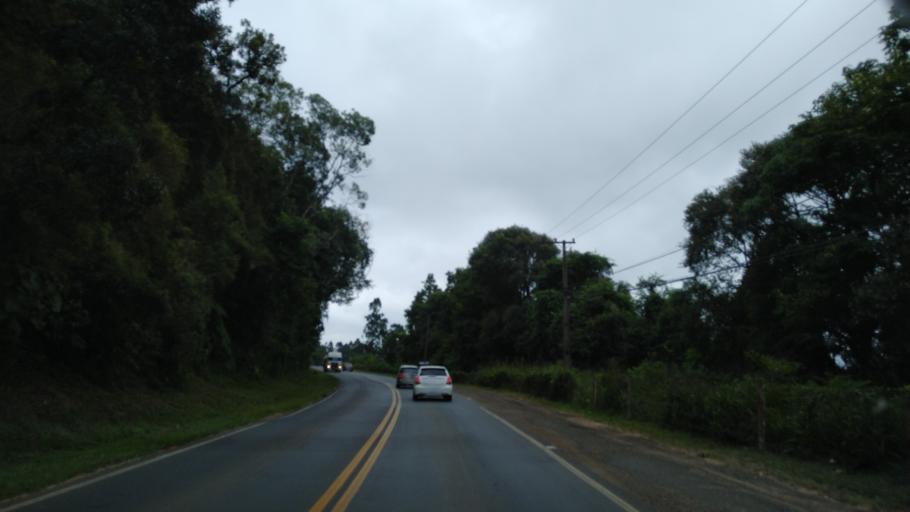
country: BR
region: Parana
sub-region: Uniao Da Vitoria
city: Uniao da Vitoria
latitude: -26.2284
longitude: -51.1271
